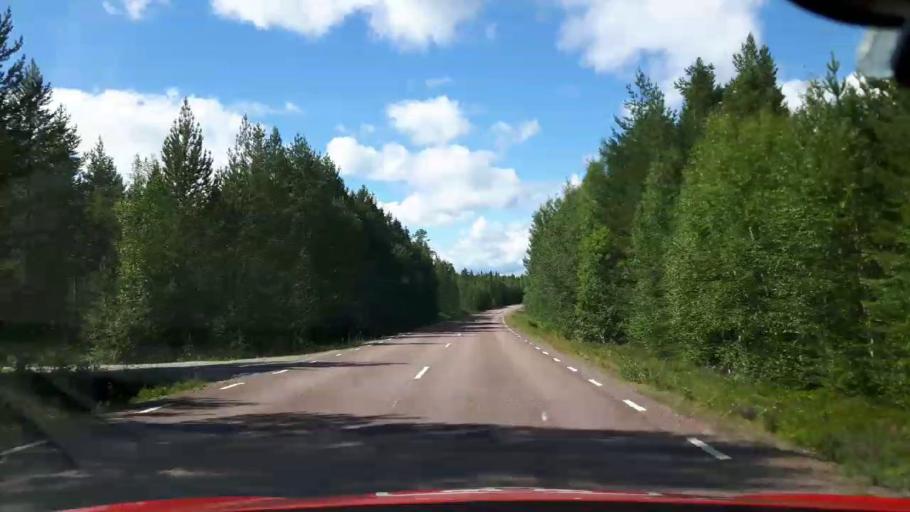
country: SE
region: Jaemtland
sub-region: Harjedalens Kommun
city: Sveg
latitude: 61.9990
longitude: 14.2613
